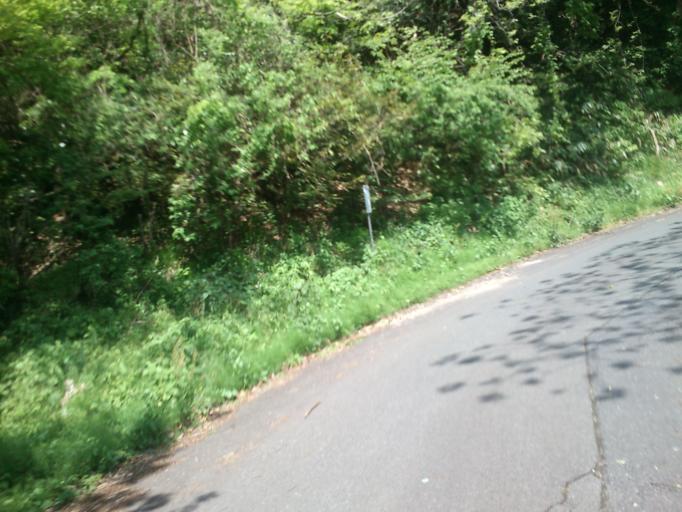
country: JP
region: Kyoto
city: Miyazu
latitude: 35.7006
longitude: 135.1553
